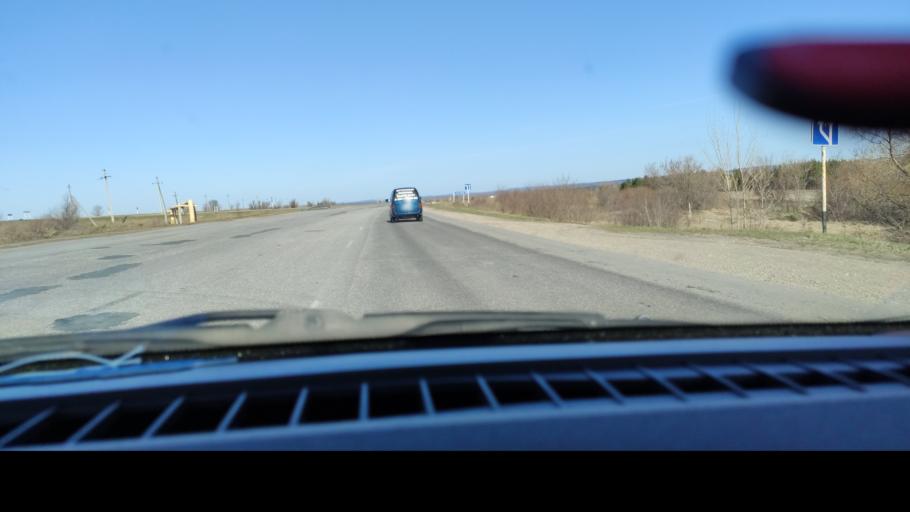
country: RU
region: Samara
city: Varlamovo
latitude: 53.1240
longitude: 48.2962
